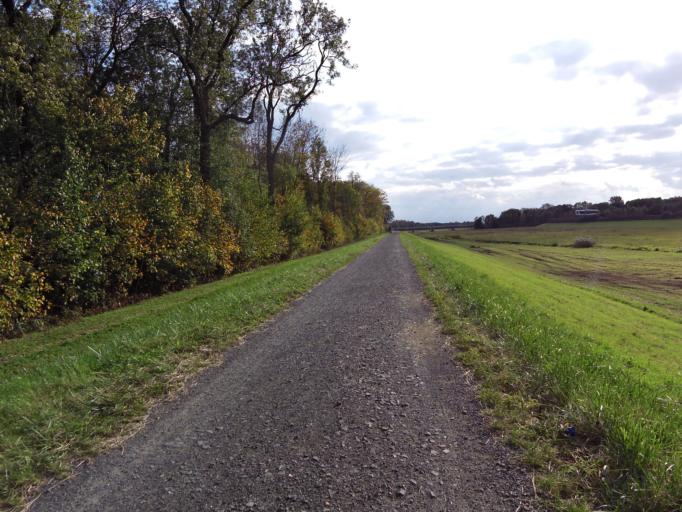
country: DE
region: Saxony
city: Markkleeberg
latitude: 51.3048
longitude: 12.3439
